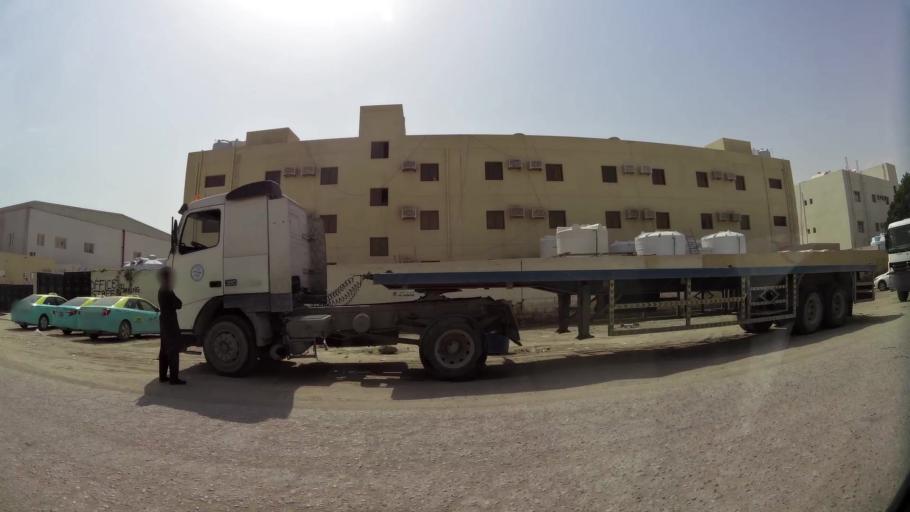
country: QA
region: Al Wakrah
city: Al Wukayr
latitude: 25.1663
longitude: 51.4583
